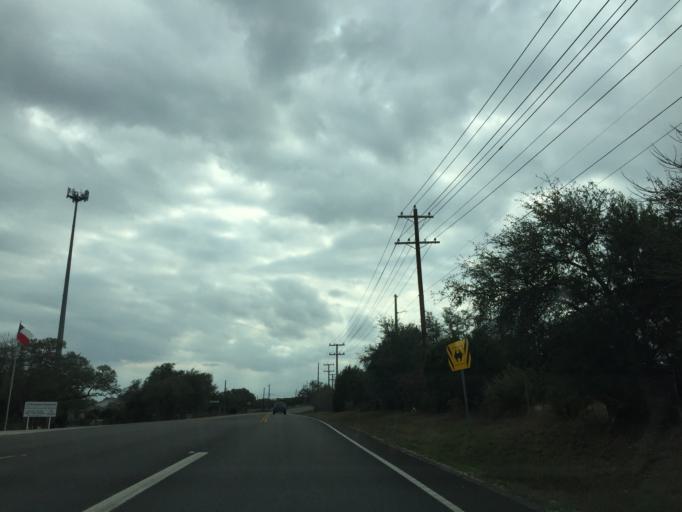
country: US
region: Texas
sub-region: Travis County
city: Shady Hollow
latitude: 30.1700
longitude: -97.9385
